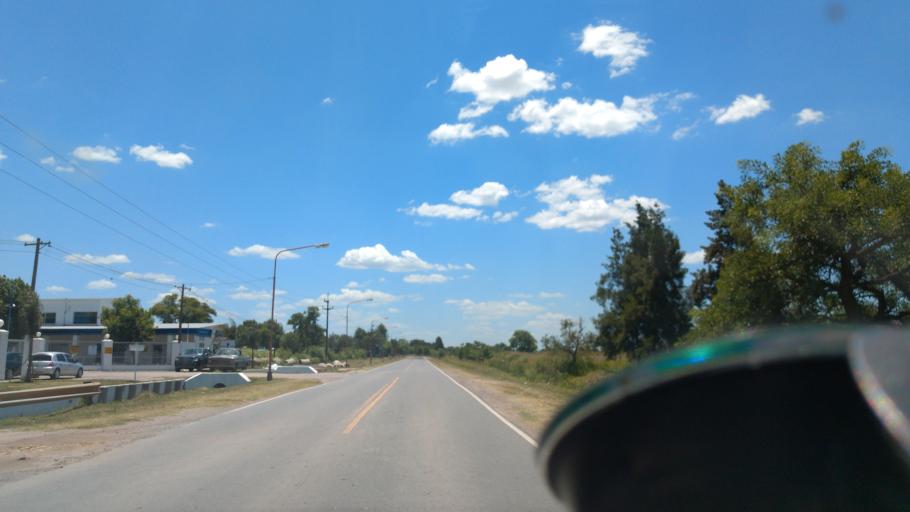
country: AR
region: Santa Fe
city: Laguna Paiva
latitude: -31.3187
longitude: -60.6586
